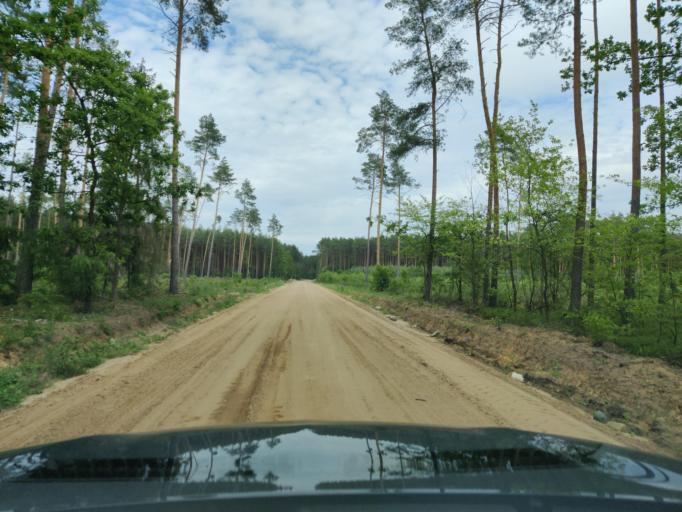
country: PL
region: Masovian Voivodeship
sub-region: Powiat pultuski
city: Pultusk
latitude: 52.7229
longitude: 21.1525
